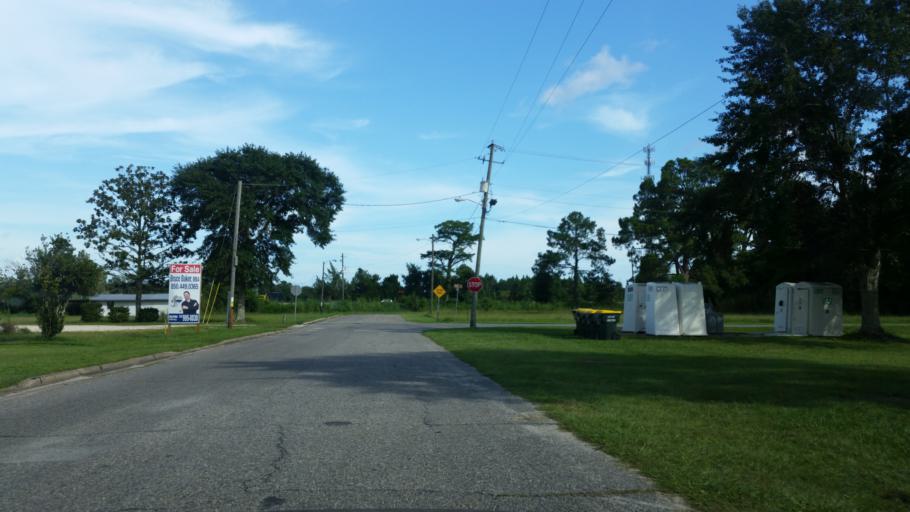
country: US
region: Florida
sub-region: Santa Rosa County
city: Milton
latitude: 30.6219
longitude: -87.0350
